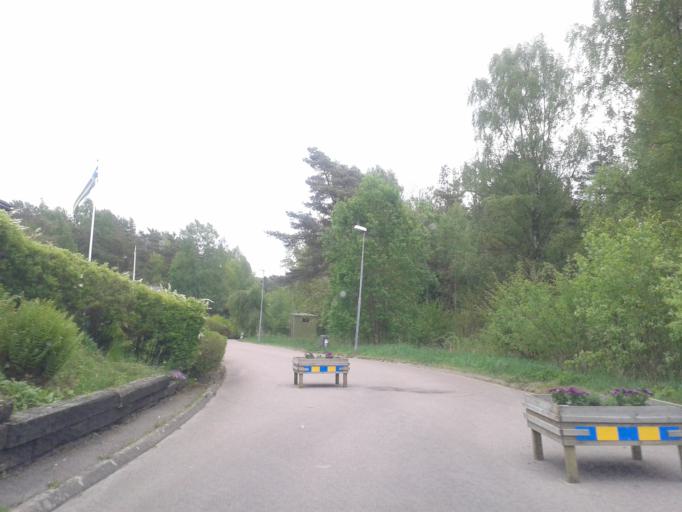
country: SE
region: Vaestra Goetaland
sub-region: Kungalvs Kommun
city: Kungalv
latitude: 57.8524
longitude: 11.9893
